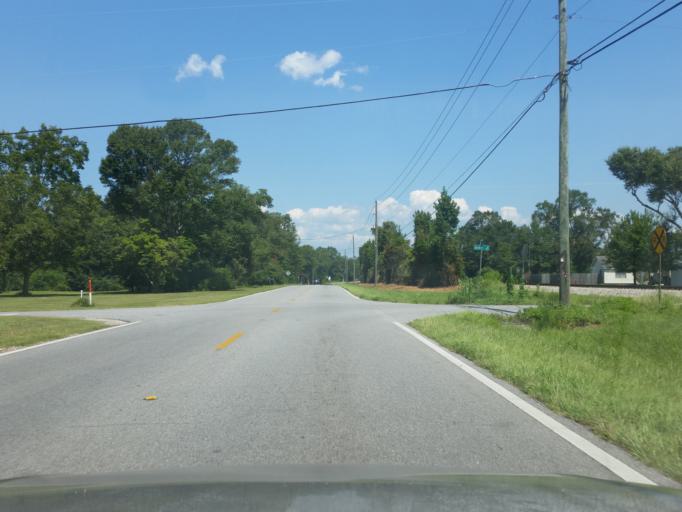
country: US
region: Florida
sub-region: Escambia County
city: Gonzalez
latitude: 30.5894
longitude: -87.3042
